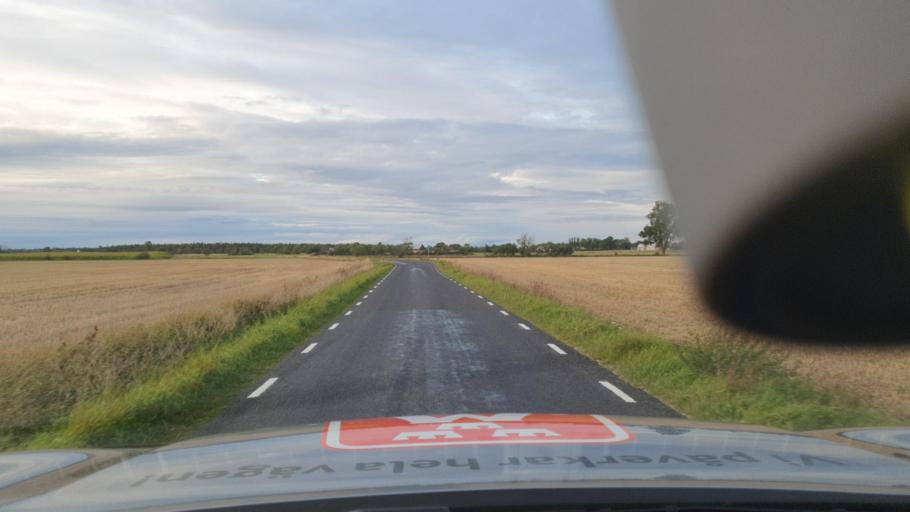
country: SE
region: Gotland
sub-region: Gotland
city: Visby
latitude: 57.6288
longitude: 18.4713
